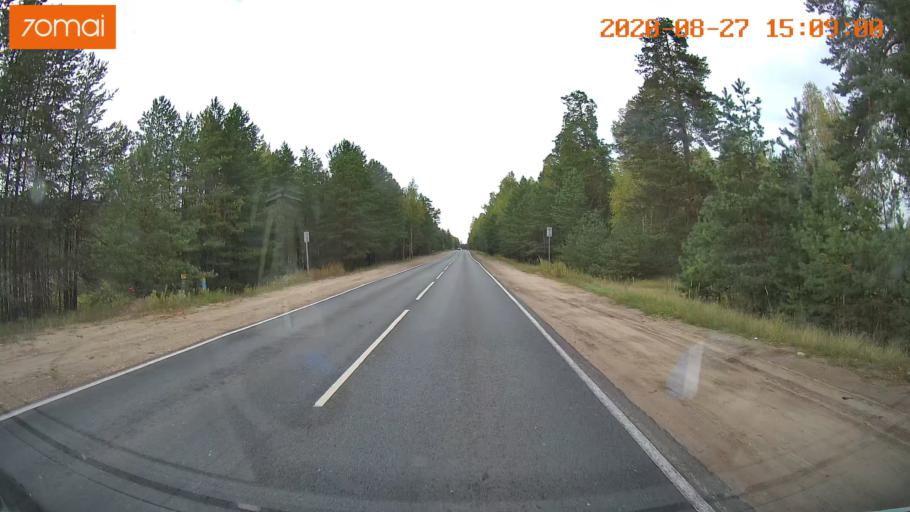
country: RU
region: Vladimir
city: Kurlovo
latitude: 55.4996
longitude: 40.5734
